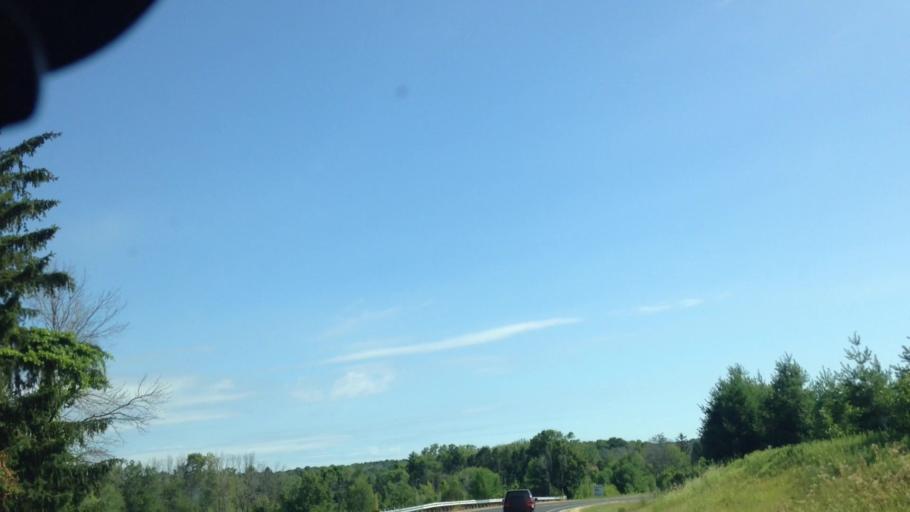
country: US
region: Wisconsin
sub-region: Washington County
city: Slinger
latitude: 43.3731
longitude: -88.2563
